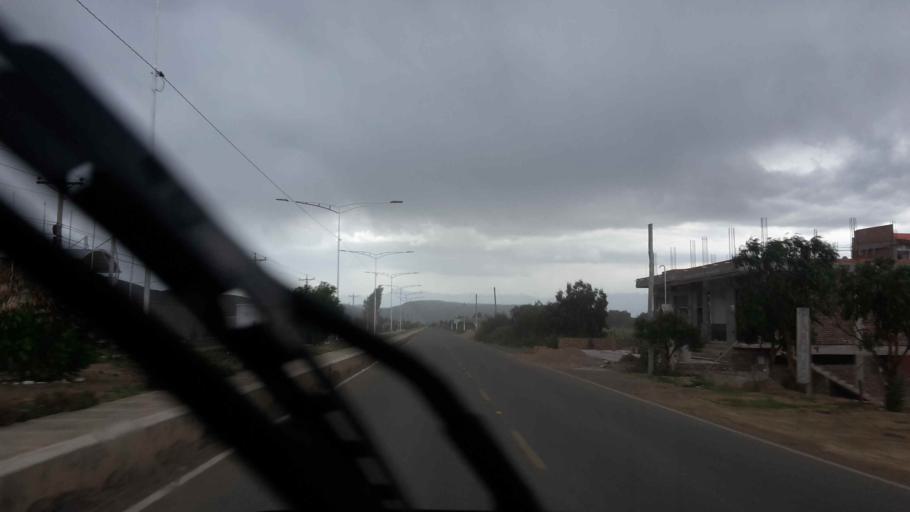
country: BO
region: Cochabamba
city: Tarata
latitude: -17.5982
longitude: -66.0379
